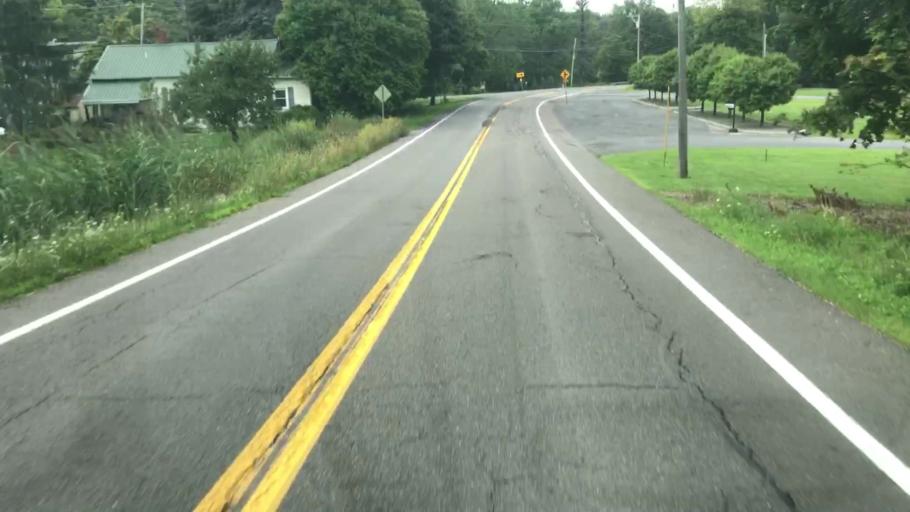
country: US
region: New York
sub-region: Onondaga County
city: Skaneateles
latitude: 42.9805
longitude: -76.4471
